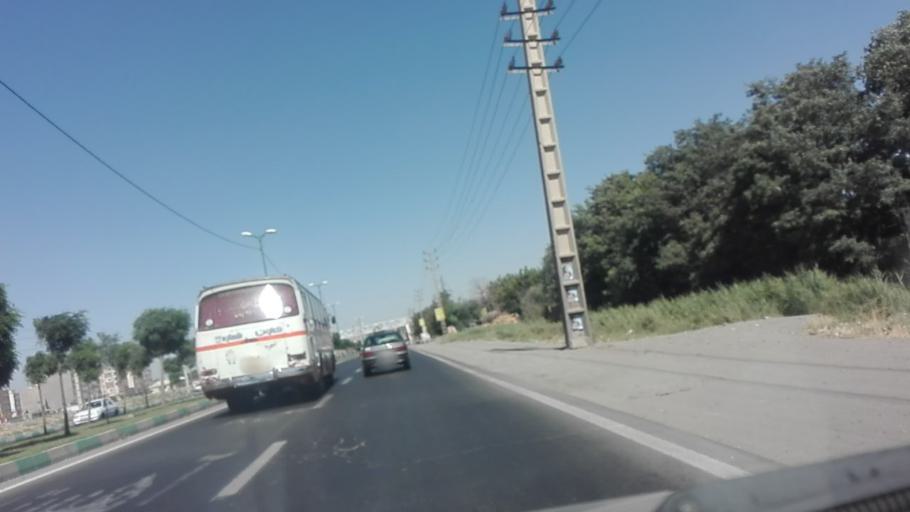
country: IR
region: Tehran
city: Shahre Jadide Andisheh
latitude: 35.6547
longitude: 51.0212
